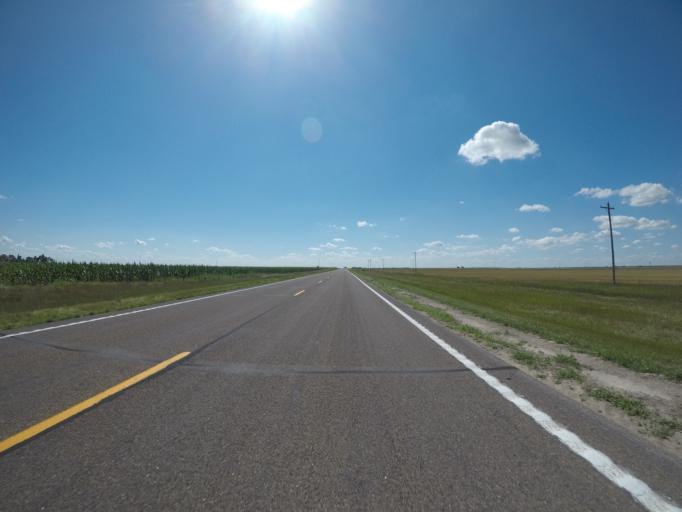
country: US
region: Nebraska
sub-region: Chase County
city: Imperial
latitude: 40.5378
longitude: -101.9085
